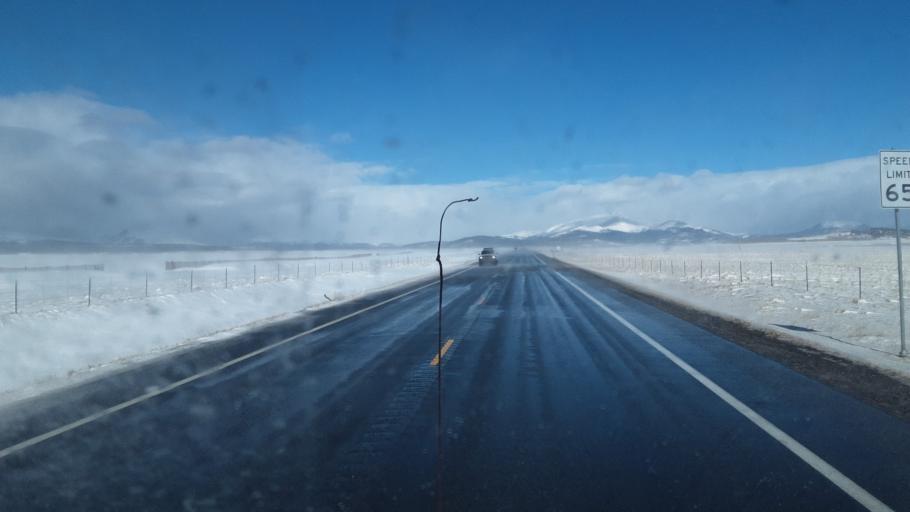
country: US
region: Colorado
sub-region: Park County
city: Fairplay
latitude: 39.1552
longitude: -105.9997
